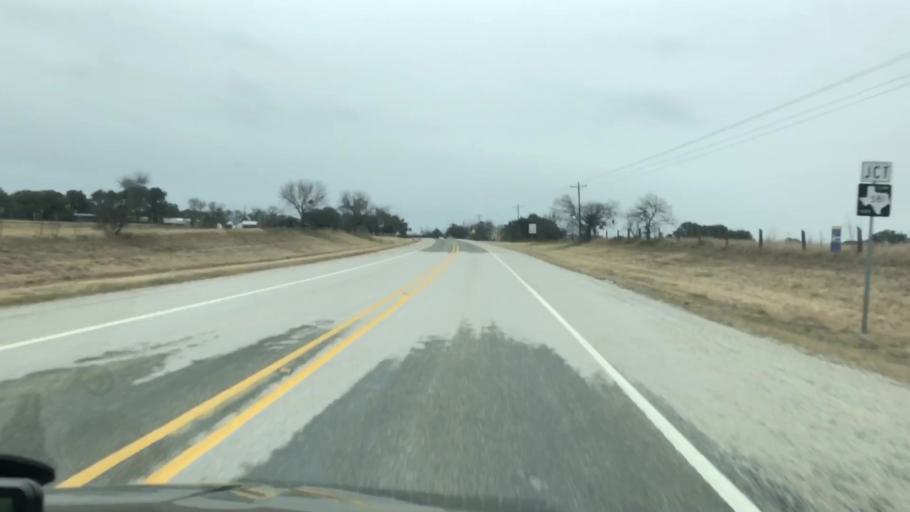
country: US
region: Texas
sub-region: Lampasas County
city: Lampasas
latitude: 31.2968
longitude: -98.1688
